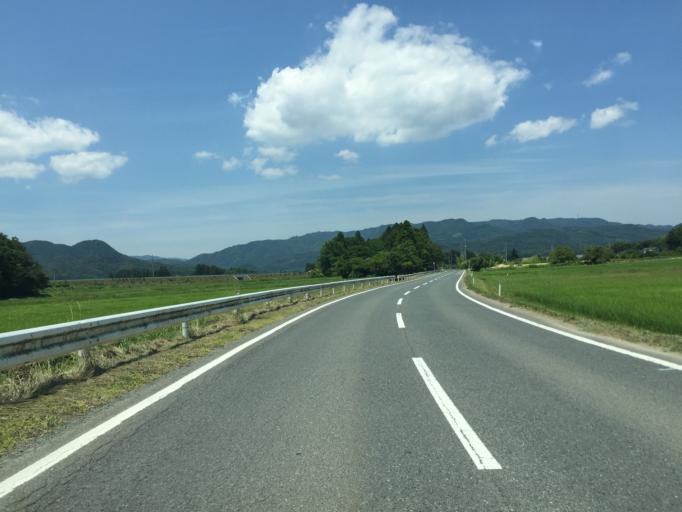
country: JP
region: Miyagi
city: Marumori
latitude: 37.7714
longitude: 140.9072
